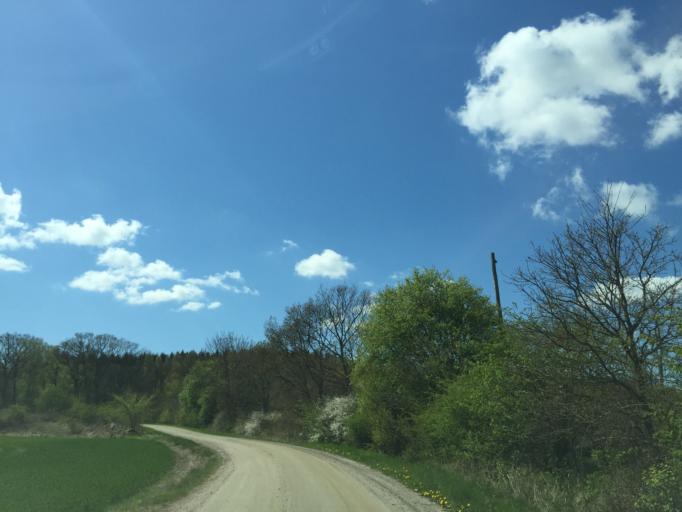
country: SE
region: Skane
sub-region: Lunds Kommun
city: Genarp
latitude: 55.7031
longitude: 13.3689
